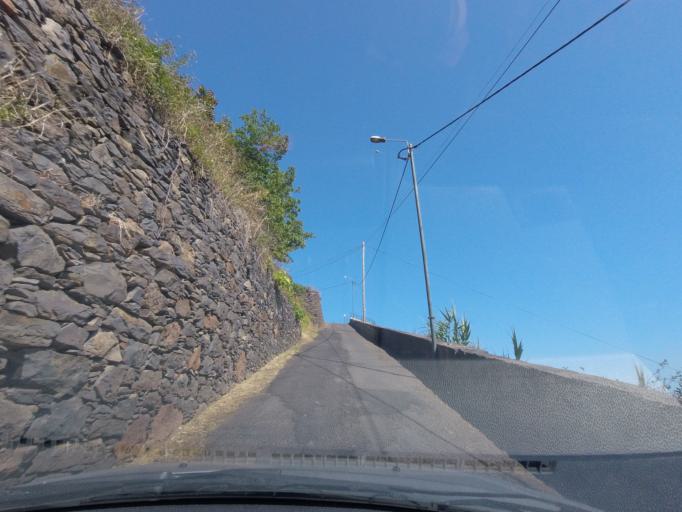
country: PT
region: Madeira
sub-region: Funchal
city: Nossa Senhora do Monte
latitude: 32.6647
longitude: -16.9007
